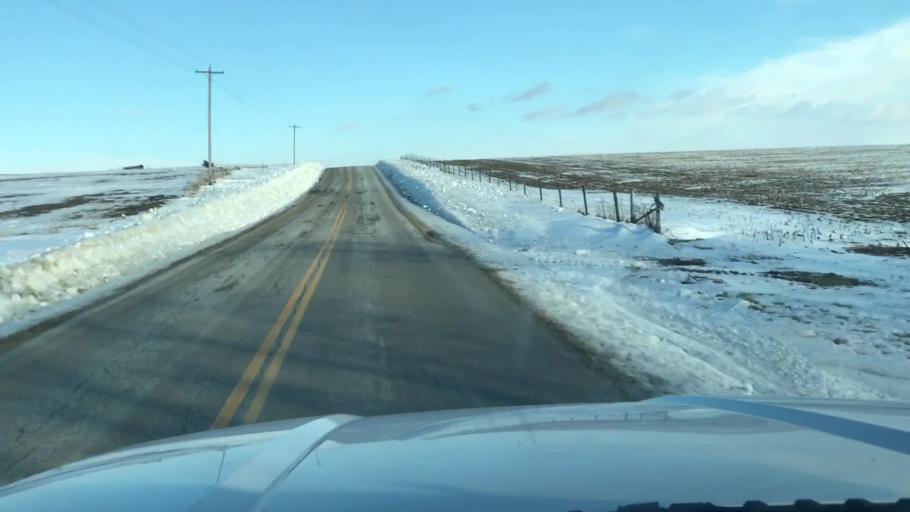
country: US
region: Missouri
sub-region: Holt County
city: Oregon
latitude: 40.1006
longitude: -94.9867
